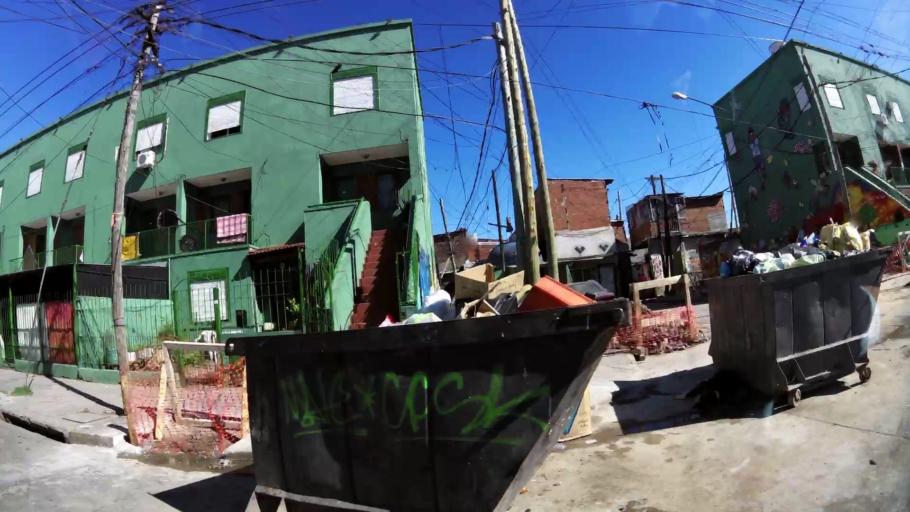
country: AR
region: Buenos Aires
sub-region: Partido de General San Martin
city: General San Martin
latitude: -34.5491
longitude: -58.5224
